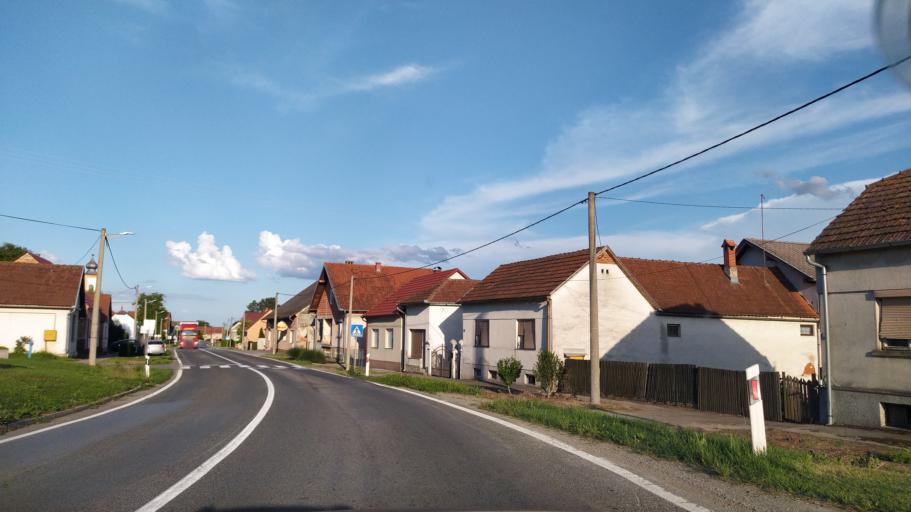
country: HR
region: Virovitick-Podravska
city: Cacinci
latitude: 45.6135
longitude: 17.8052
